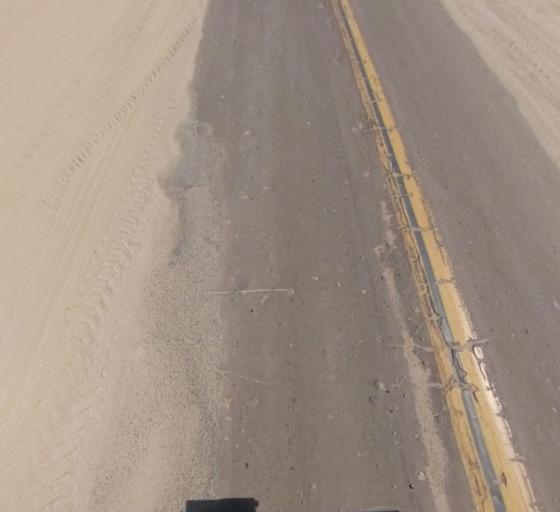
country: US
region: California
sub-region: Fresno County
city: Biola
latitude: 36.8226
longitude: -120.0428
